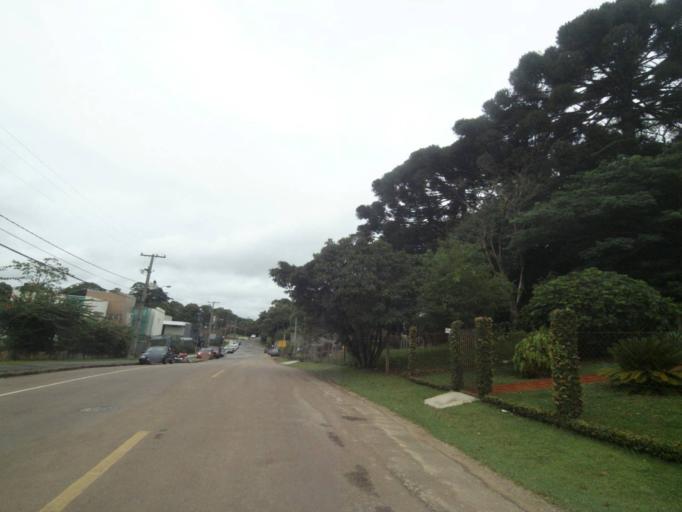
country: BR
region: Parana
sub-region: Curitiba
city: Curitiba
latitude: -25.4527
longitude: -49.3373
